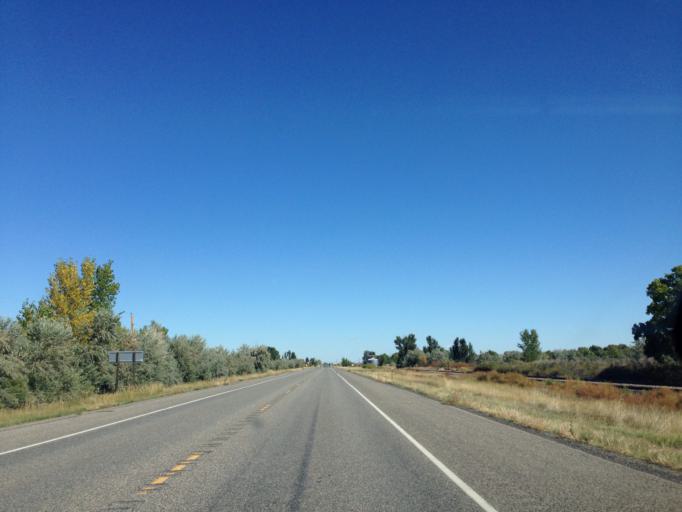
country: US
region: Montana
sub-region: Yellowstone County
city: Laurel
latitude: 45.3825
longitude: -108.9120
